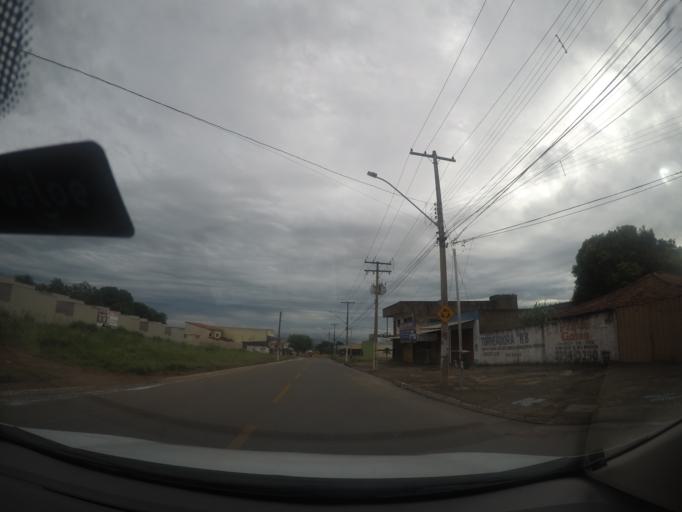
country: BR
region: Goias
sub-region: Goiania
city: Goiania
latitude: -16.6087
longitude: -49.3177
